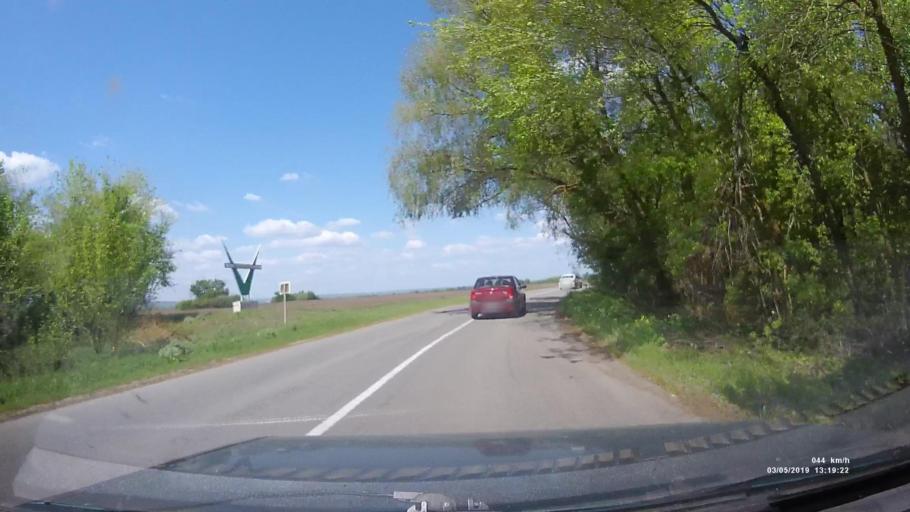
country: RU
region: Rostov
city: Semikarakorsk
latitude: 47.5371
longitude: 40.7478
